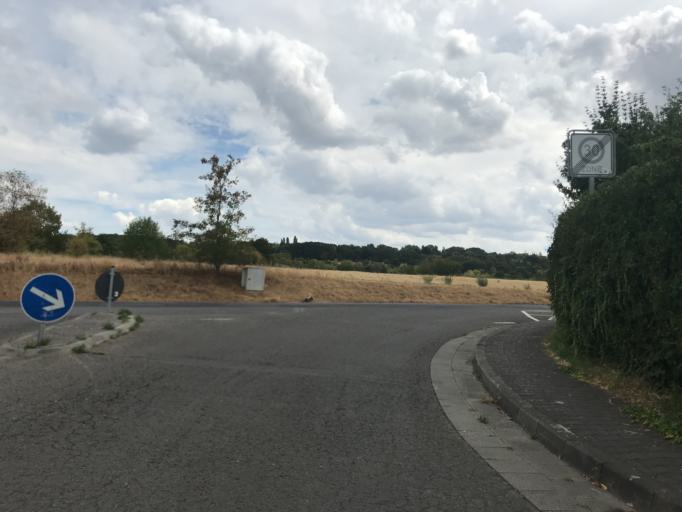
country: DE
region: Rheinland-Pfalz
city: Budenheim
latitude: 50.0049
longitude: 8.1401
